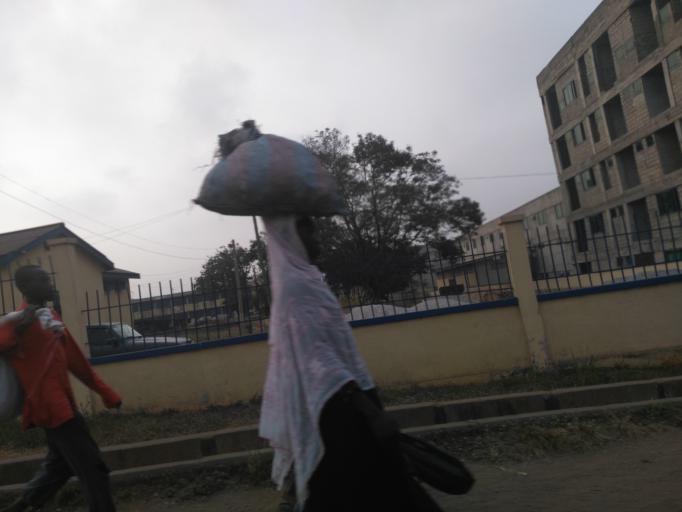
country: GH
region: Ashanti
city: Kumasi
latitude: 6.6885
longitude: -1.5956
